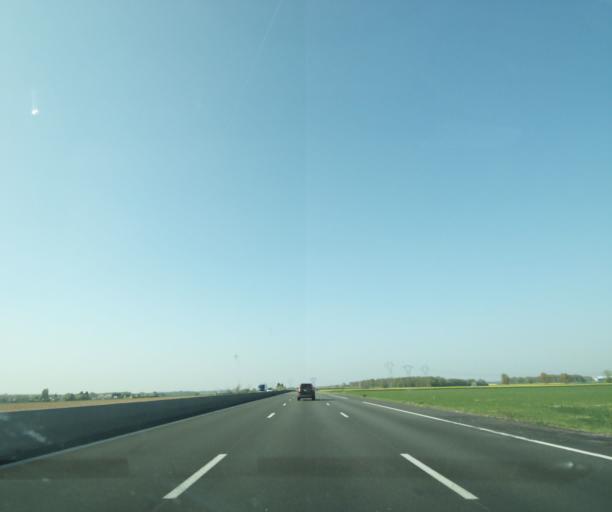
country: FR
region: Ile-de-France
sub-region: Departement de Seine-et-Marne
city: Ponthierry
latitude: 48.5217
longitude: 2.5040
